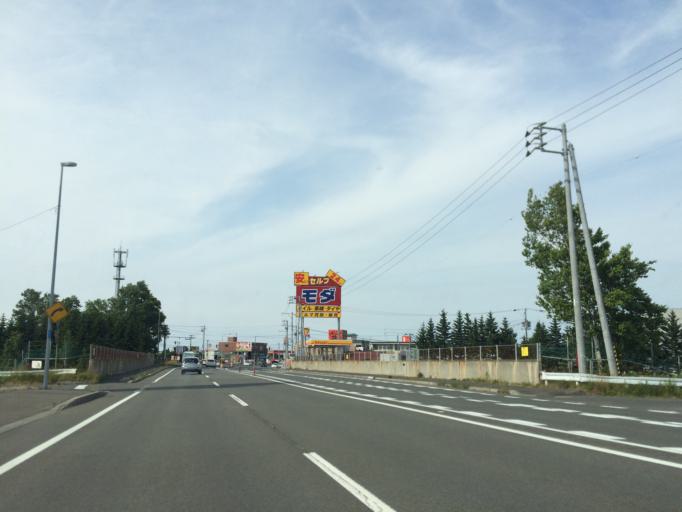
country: JP
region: Hokkaido
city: Ebetsu
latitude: 43.0858
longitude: 141.5155
